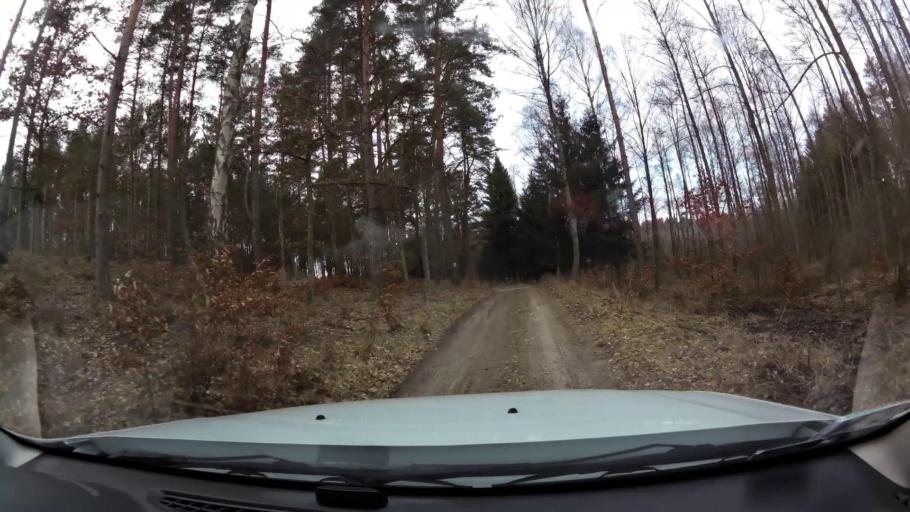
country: PL
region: West Pomeranian Voivodeship
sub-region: Powiat drawski
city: Drawsko Pomorskie
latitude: 53.5326
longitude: 15.6997
